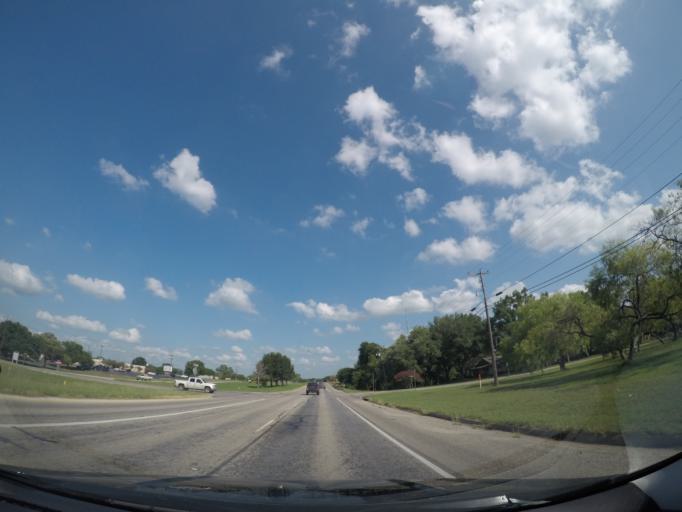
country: US
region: Texas
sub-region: Gonzales County
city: Gonzales
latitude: 29.5177
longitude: -97.4316
